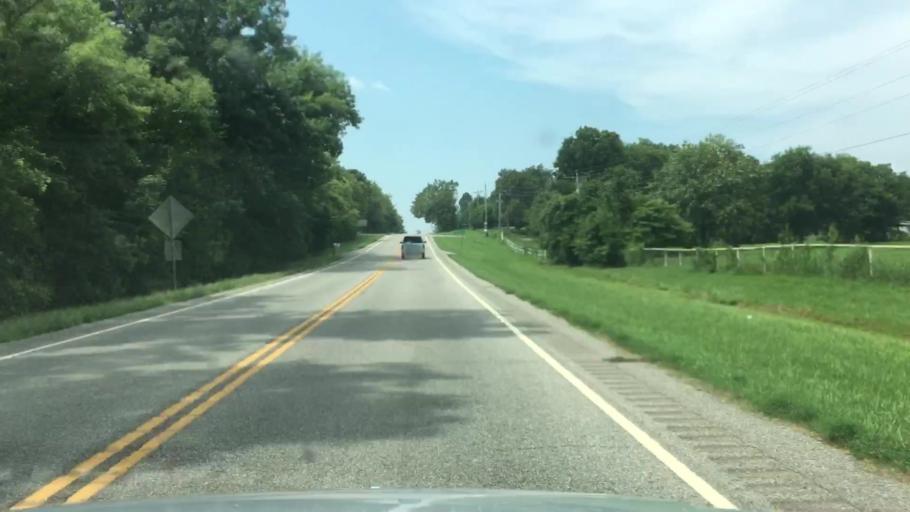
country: US
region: Oklahoma
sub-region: Wagoner County
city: Wagoner
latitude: 35.9297
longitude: -95.2413
